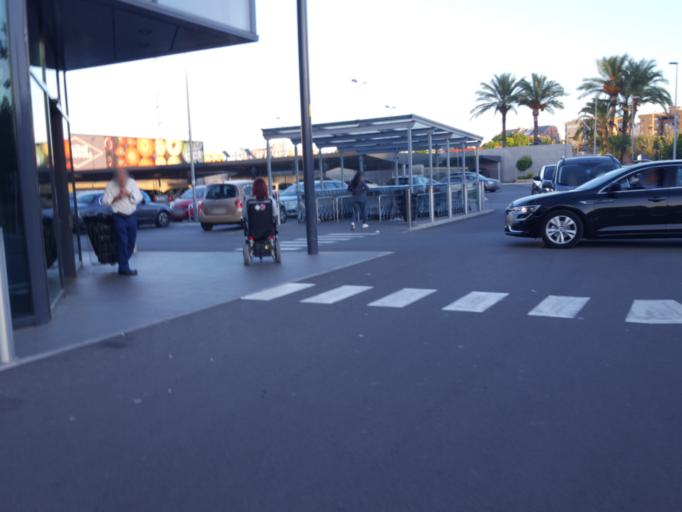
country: ES
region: Murcia
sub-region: Murcia
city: Murcia
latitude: 38.0022
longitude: -1.1449
